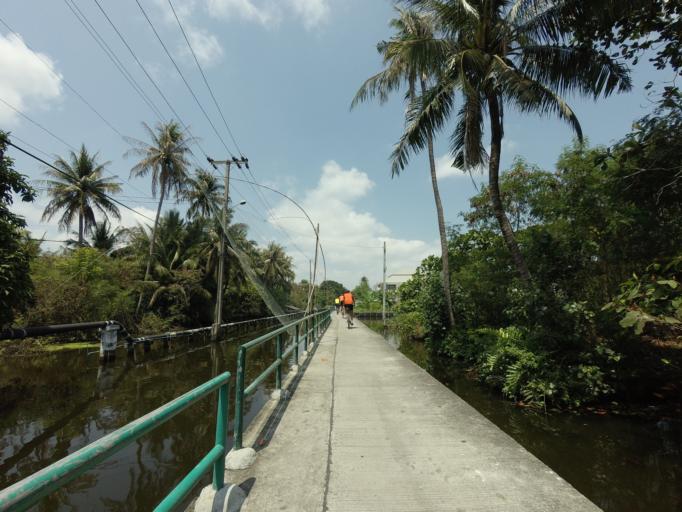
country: TH
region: Bangkok
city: Chom Thong
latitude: 13.6418
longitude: 100.4733
